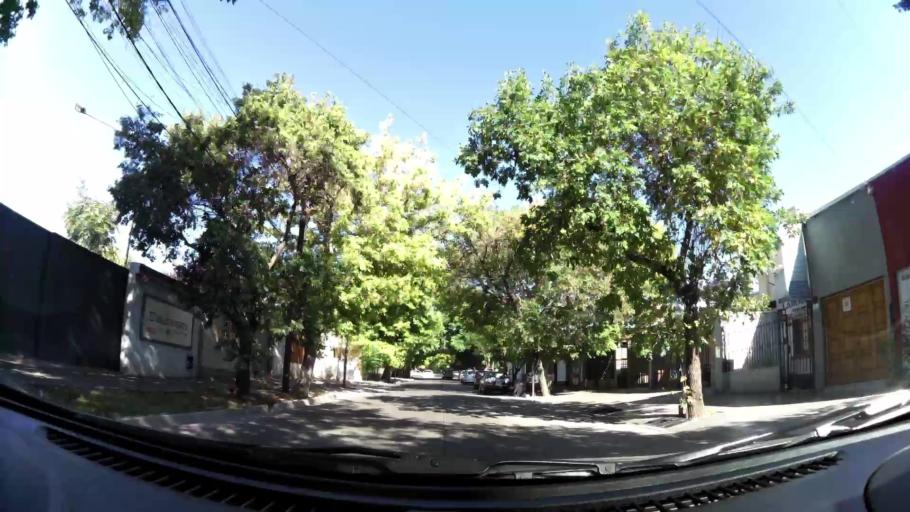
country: AR
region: Mendoza
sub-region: Departamento de Godoy Cruz
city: Godoy Cruz
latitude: -32.9238
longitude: -68.8534
